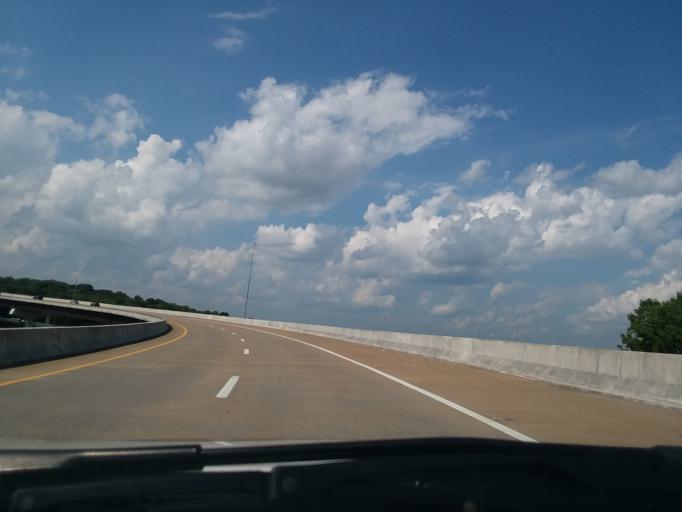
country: US
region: Tennessee
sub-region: Davidson County
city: Nashville
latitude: 36.2366
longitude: -86.7433
